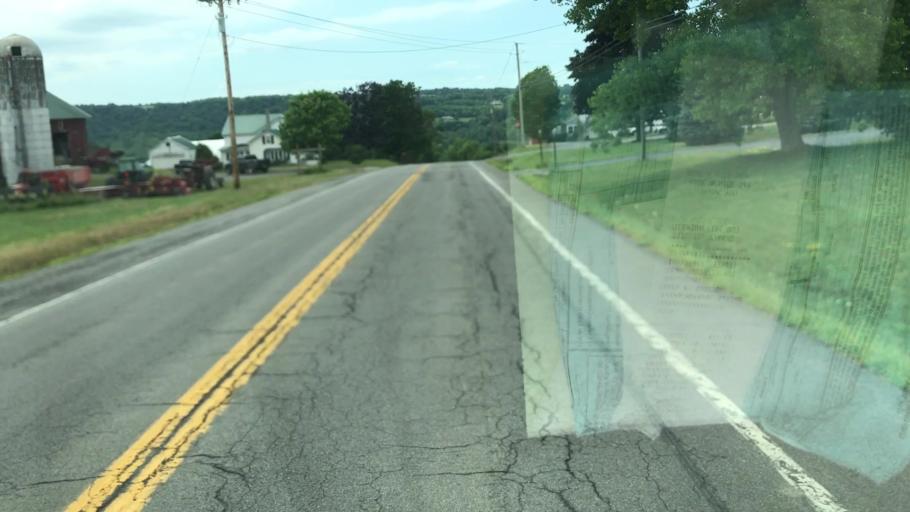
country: US
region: New York
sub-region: Onondaga County
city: Marcellus
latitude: 42.9330
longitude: -76.3168
